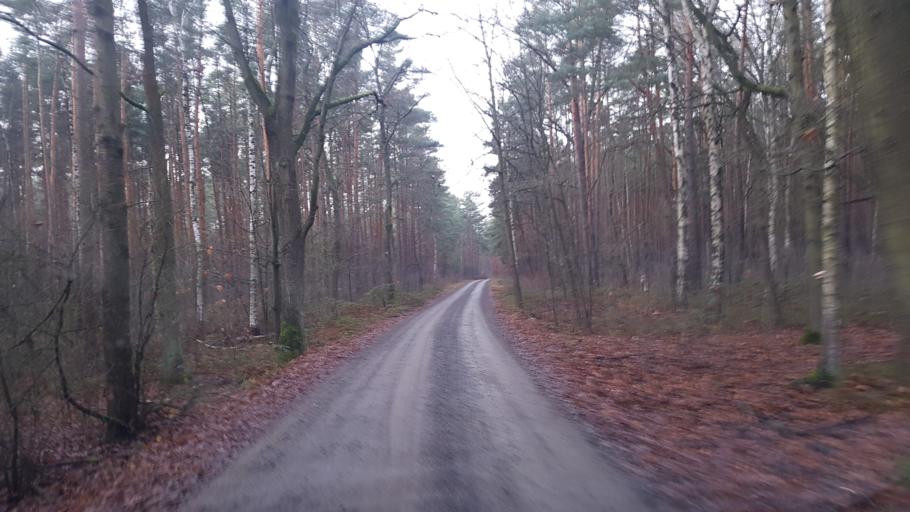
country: DE
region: Brandenburg
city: Ruckersdorf
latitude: 51.5827
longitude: 13.6035
